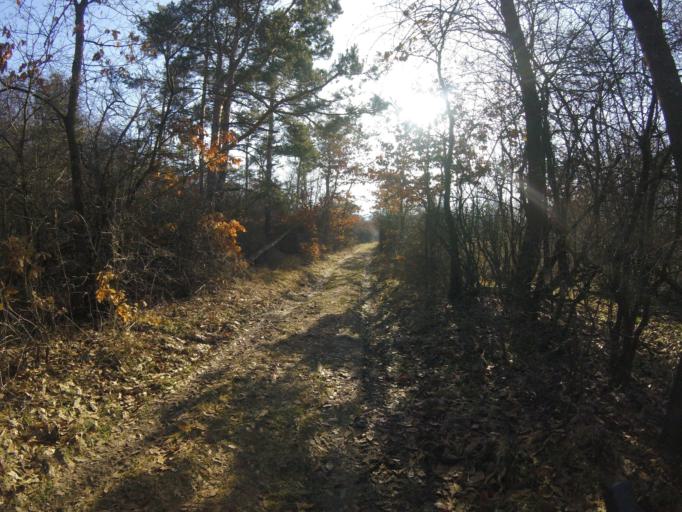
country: HU
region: Komarom-Esztergom
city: Oroszlany
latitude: 47.4779
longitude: 18.3674
